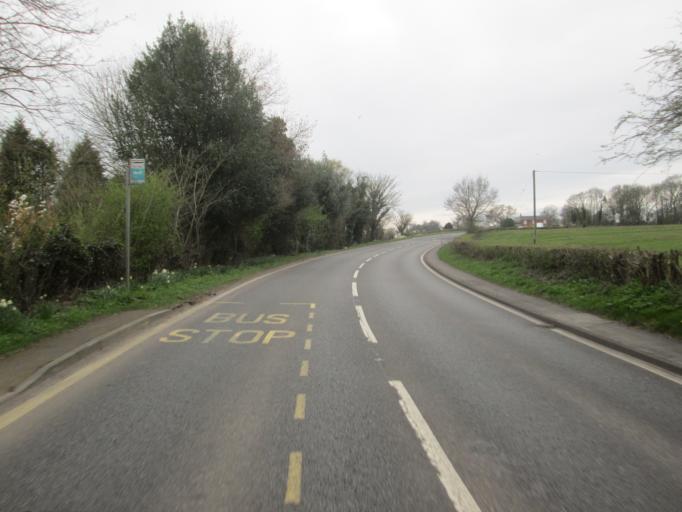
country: GB
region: England
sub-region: Derbyshire
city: Findern
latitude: 52.9404
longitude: -1.5509
